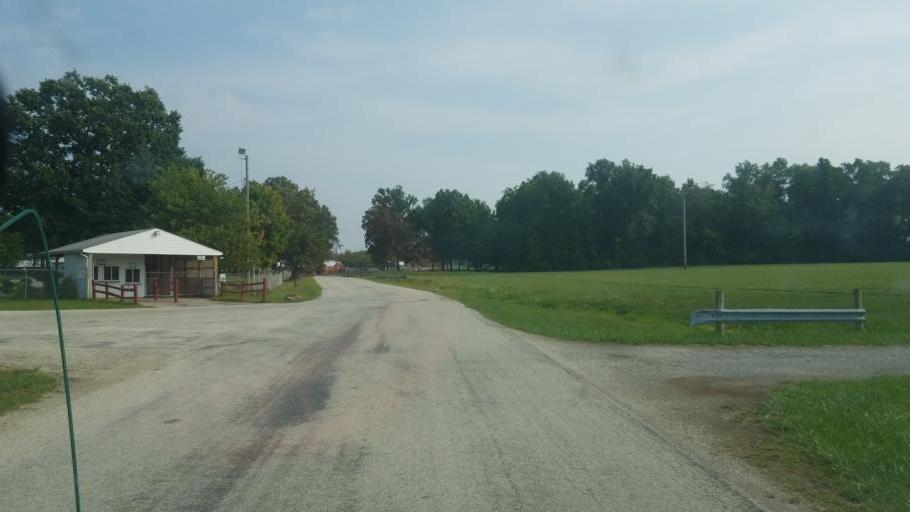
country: US
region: Ohio
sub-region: Medina County
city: Medina
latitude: 41.1348
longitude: -81.8828
